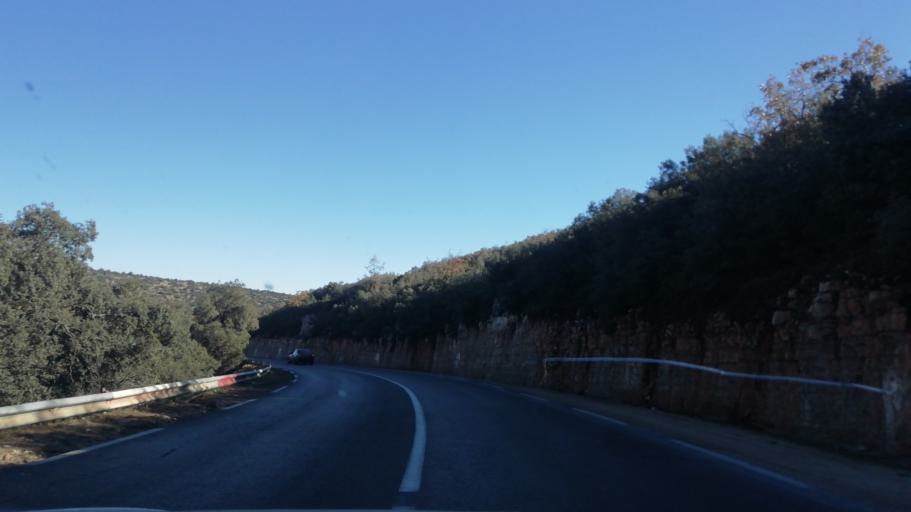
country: DZ
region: Tlemcen
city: Sebdou
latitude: 34.7404
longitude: -1.3455
